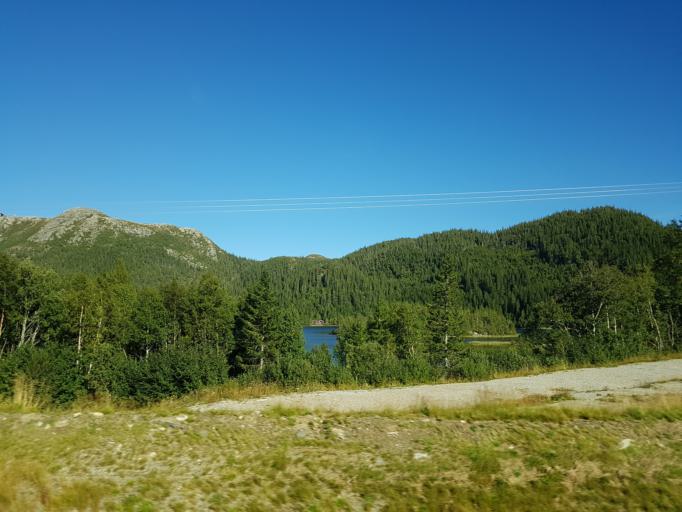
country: NO
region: Sor-Trondelag
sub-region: Afjord
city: A i Afjord
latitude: 63.6978
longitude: 10.2407
